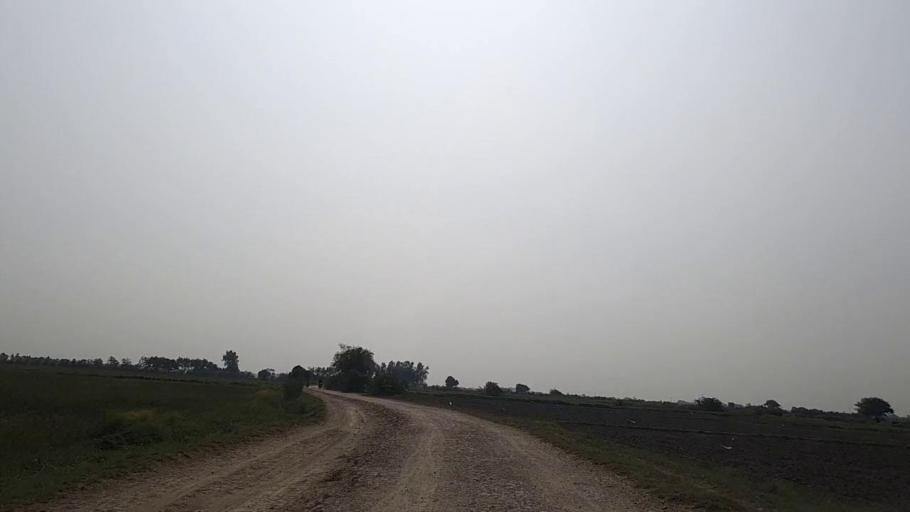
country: PK
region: Sindh
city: Mirpur Sakro
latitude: 24.6377
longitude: 67.7675
